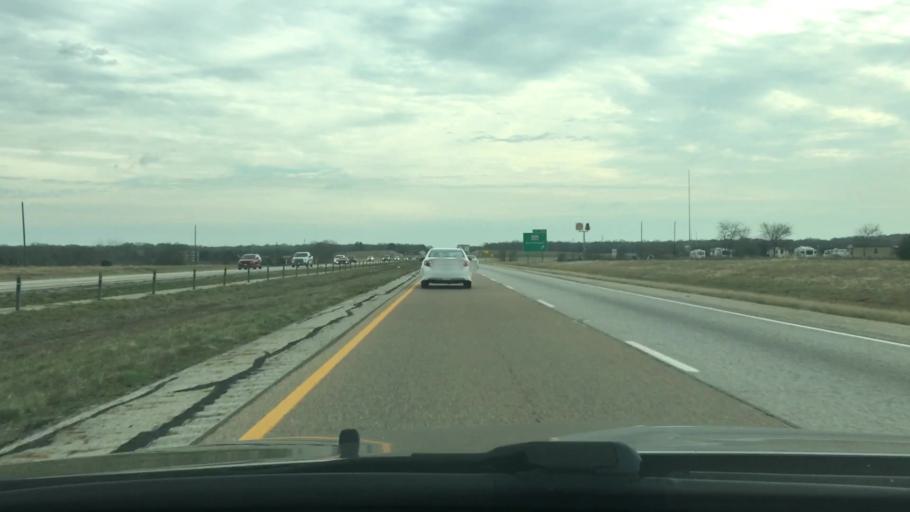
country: US
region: Texas
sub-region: Madison County
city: Madisonville
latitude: 31.0990
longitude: -95.9633
